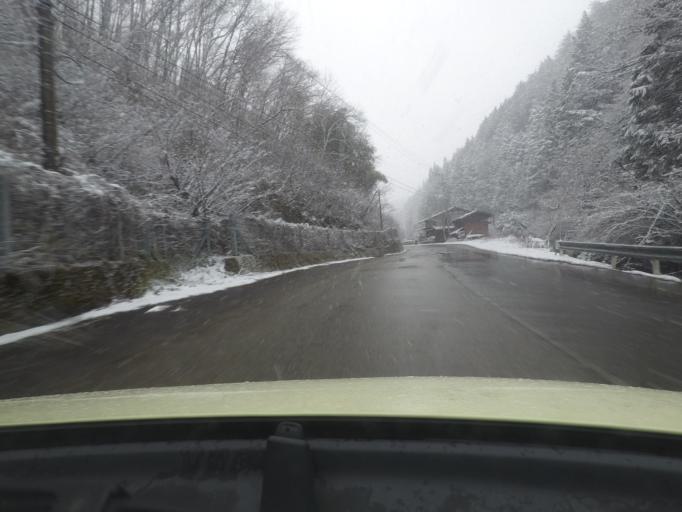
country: JP
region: Gifu
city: Takayama
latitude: 36.1380
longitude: 137.3386
